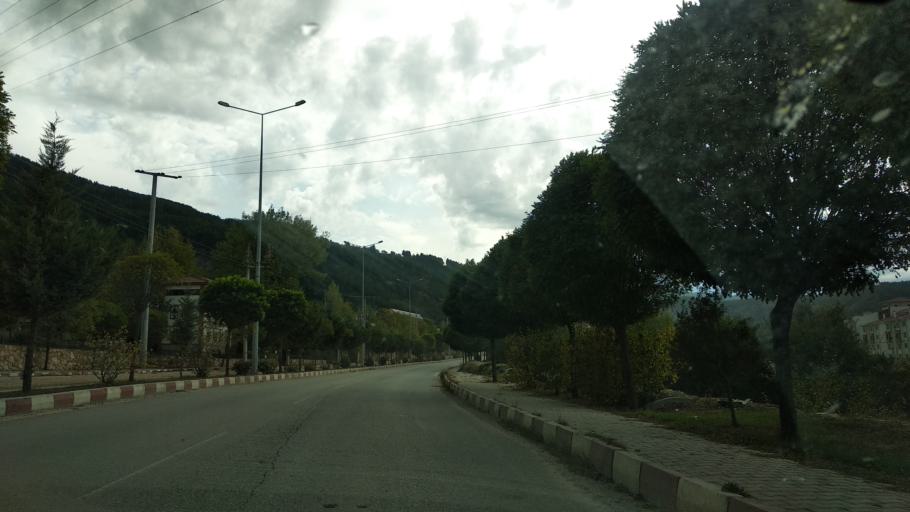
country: TR
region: Bolu
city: Mudurnu
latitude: 40.4805
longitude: 31.2095
